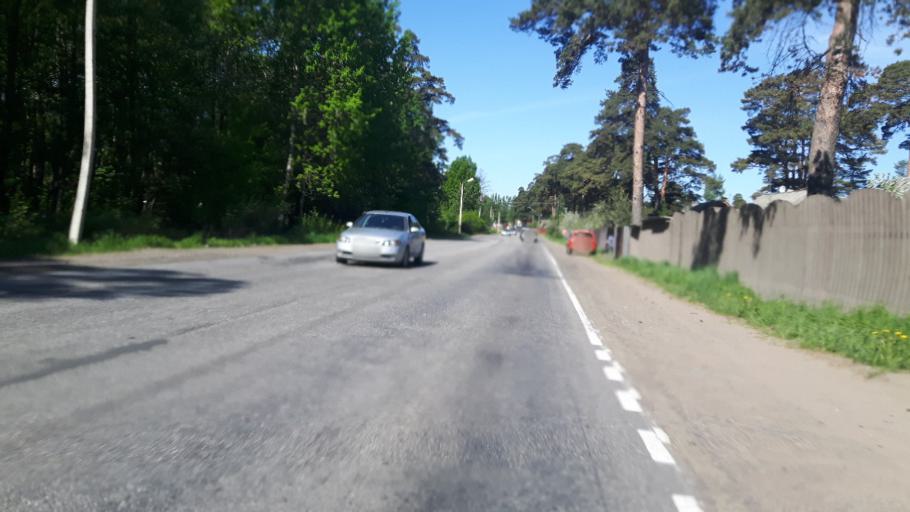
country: RU
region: Leningrad
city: Lebyazh'ye
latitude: 59.9599
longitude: 29.4366
